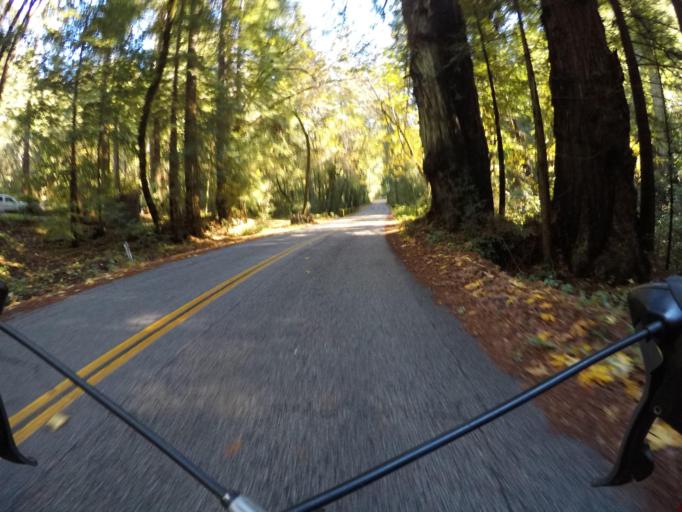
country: US
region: California
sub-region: Santa Cruz County
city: Scotts Valley
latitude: 37.0970
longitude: -121.9996
